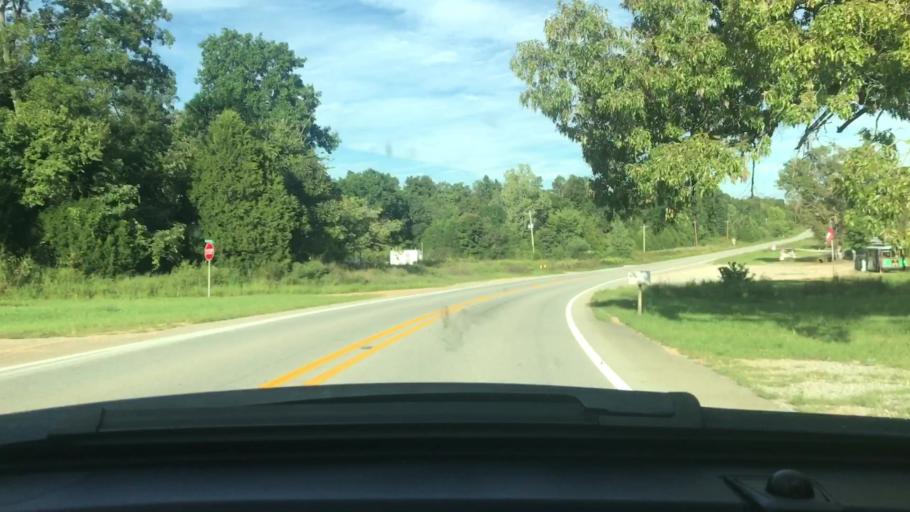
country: US
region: Arkansas
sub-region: Sharp County
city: Cherokee Village
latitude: 36.2745
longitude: -91.3510
